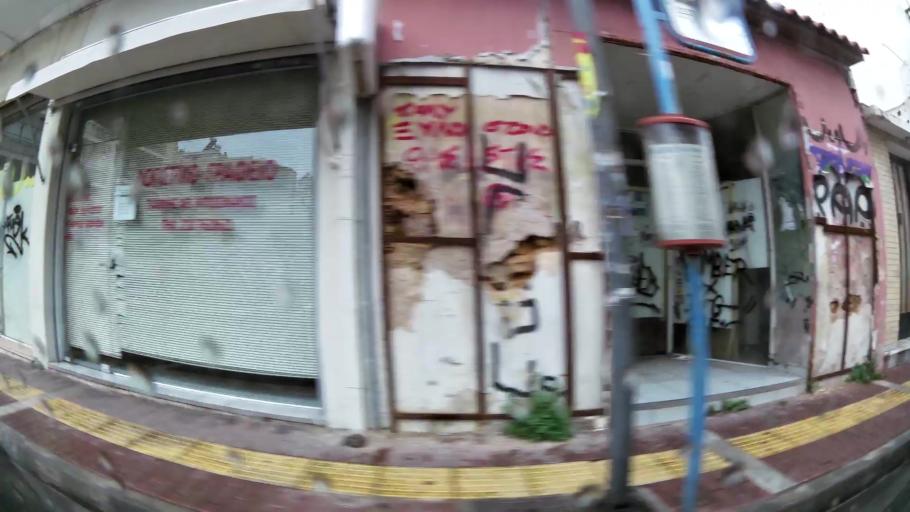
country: GR
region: Attica
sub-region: Nomarchia Athinas
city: Ymittos
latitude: 37.9534
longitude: 23.7524
